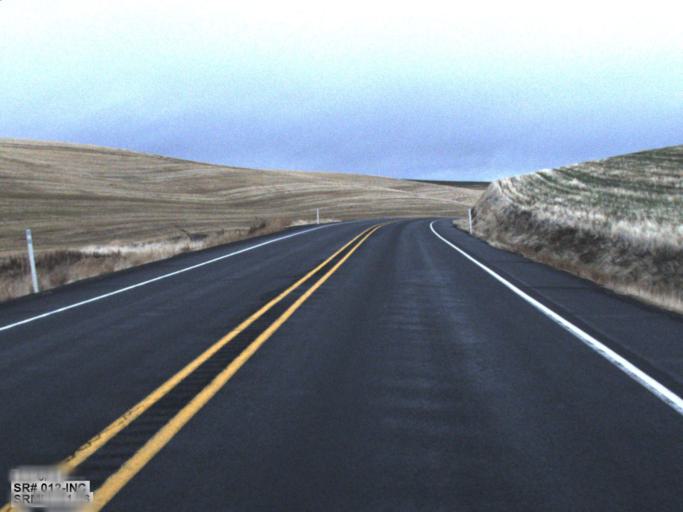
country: US
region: Washington
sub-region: Columbia County
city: Dayton
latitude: 46.3609
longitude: -117.9507
